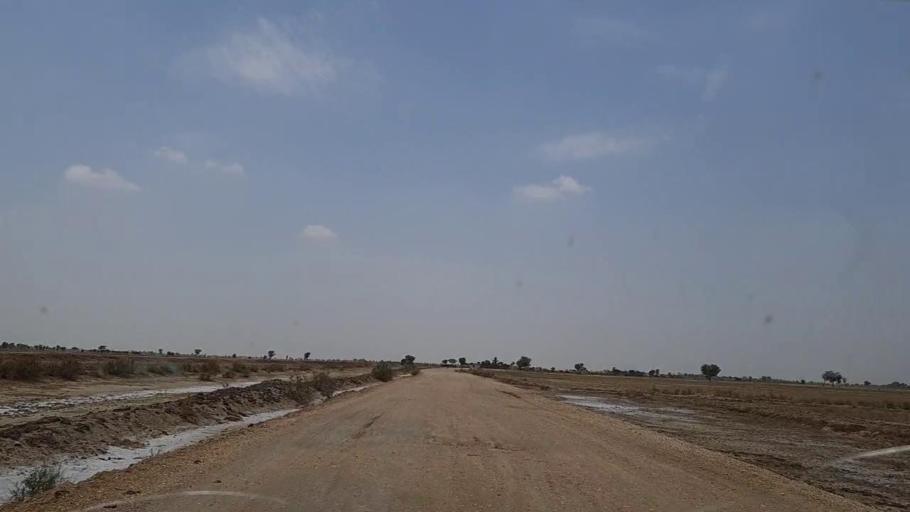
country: PK
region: Sindh
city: Phulji
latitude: 26.8006
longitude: 67.6359
